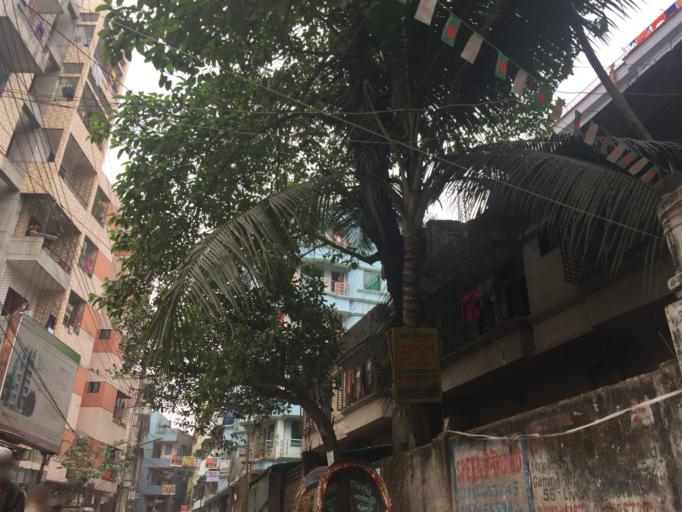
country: BD
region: Dhaka
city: Azimpur
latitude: 23.7804
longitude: 90.3656
